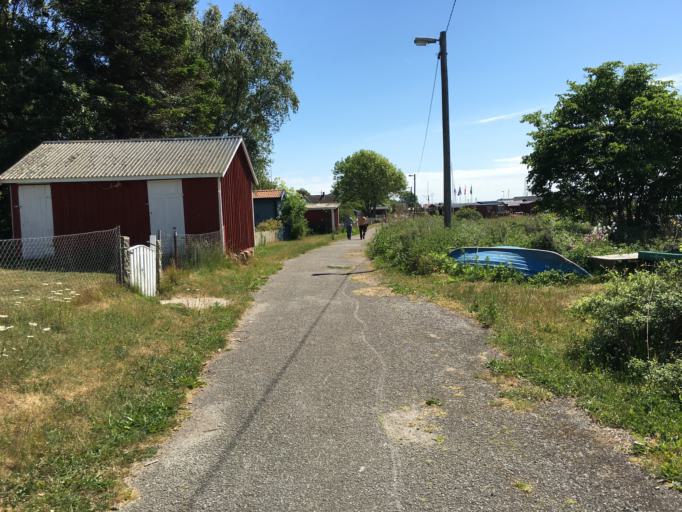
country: SE
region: Blekinge
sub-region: Karlshamns Kommun
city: Karlshamn
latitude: 56.0119
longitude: 14.8358
